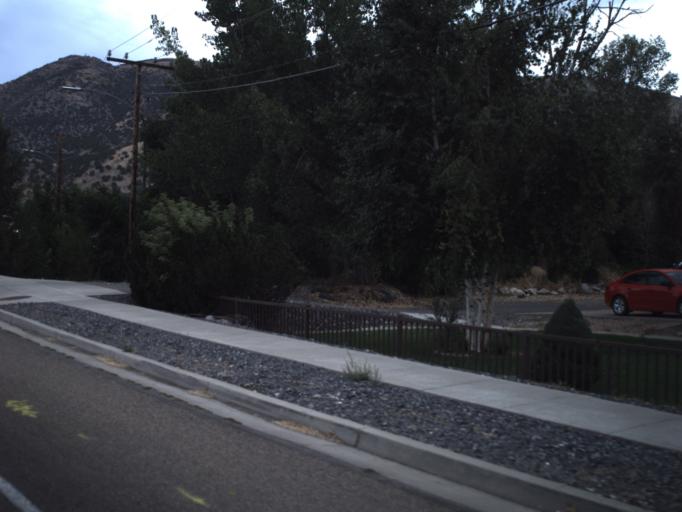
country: US
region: Utah
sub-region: Morgan County
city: Morgan
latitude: 41.0416
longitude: -111.6797
